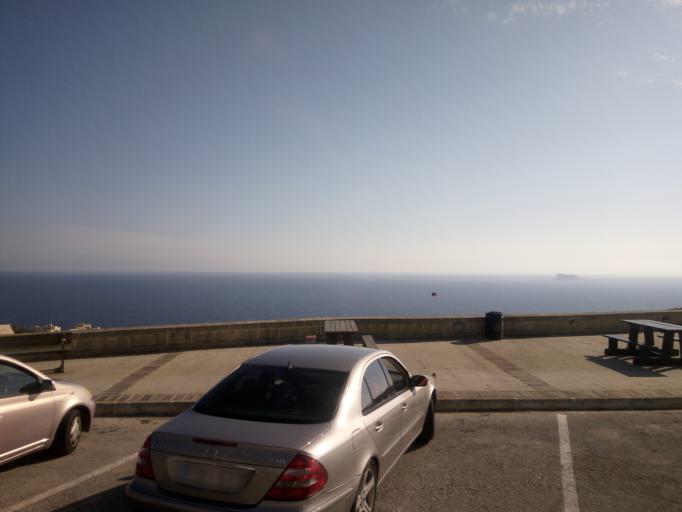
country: MT
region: Il-Qrendi
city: Qrendi
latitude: 35.8238
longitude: 14.4530
